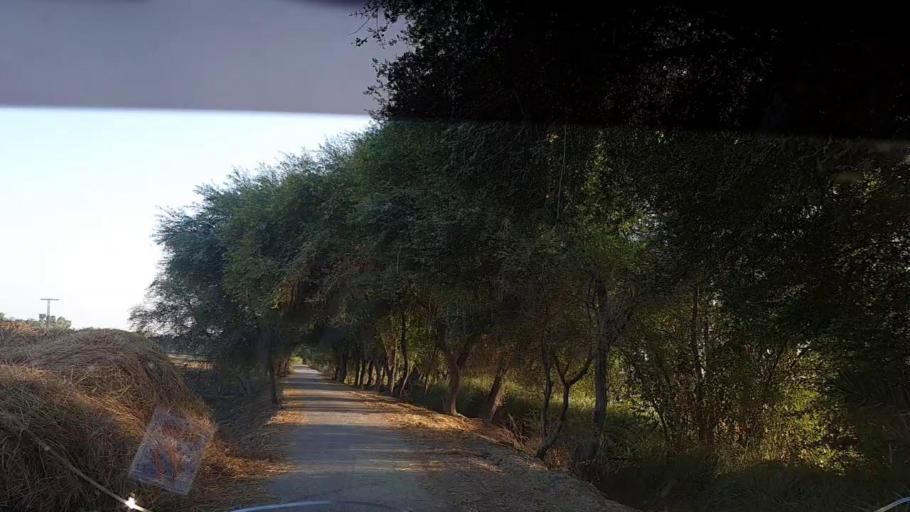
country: PK
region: Sindh
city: Ratodero
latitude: 27.8730
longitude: 68.1873
